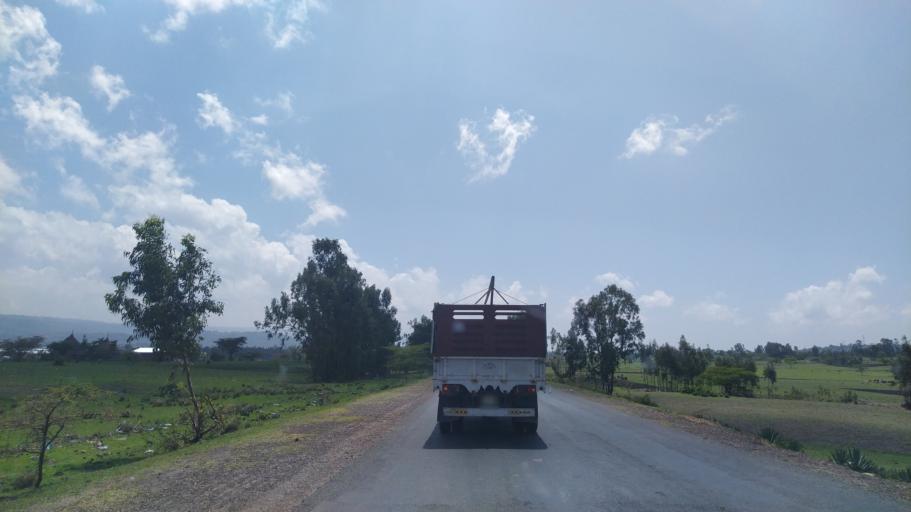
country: ET
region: Southern Nations, Nationalities, and People's Region
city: Butajira
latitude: 7.7673
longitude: 38.1366
